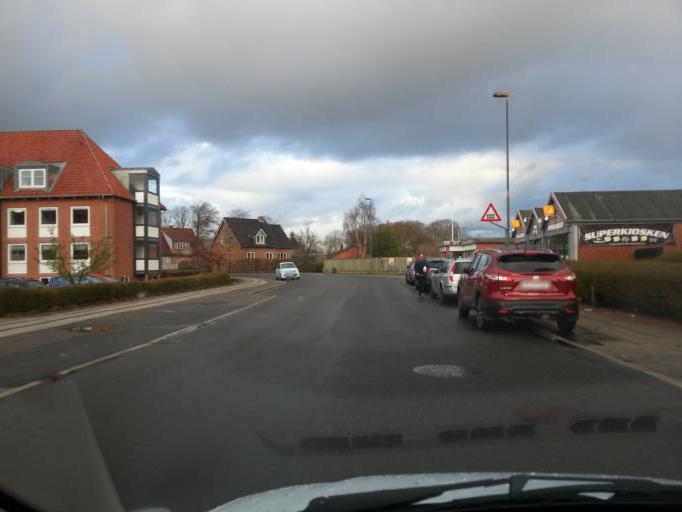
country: DK
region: Central Jutland
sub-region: Holstebro Kommune
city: Holstebro
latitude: 56.3529
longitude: 8.6093
